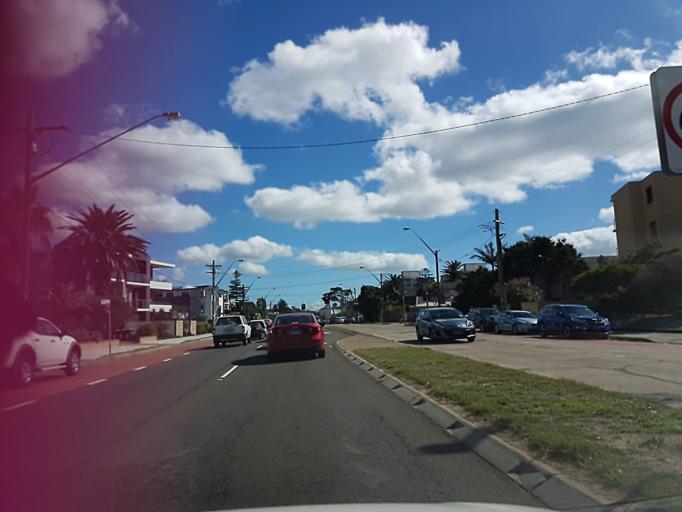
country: AU
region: New South Wales
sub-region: Warringah
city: Narrabeen
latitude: -33.7230
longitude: 151.2986
